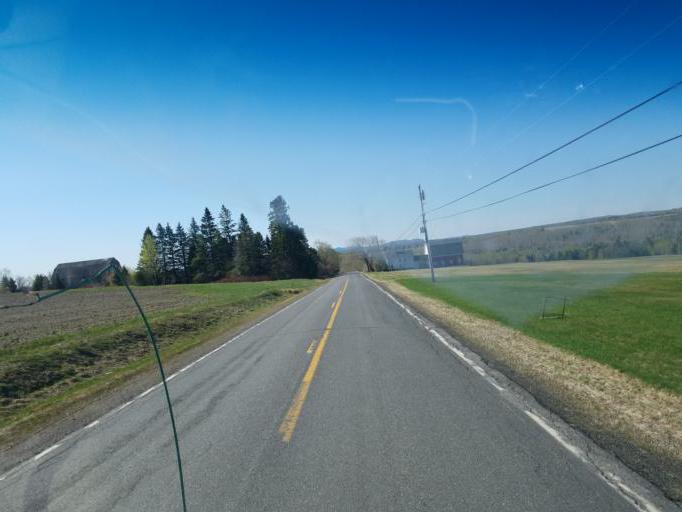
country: US
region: Maine
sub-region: Aroostook County
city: Caribou
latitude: 46.8654
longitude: -68.2087
